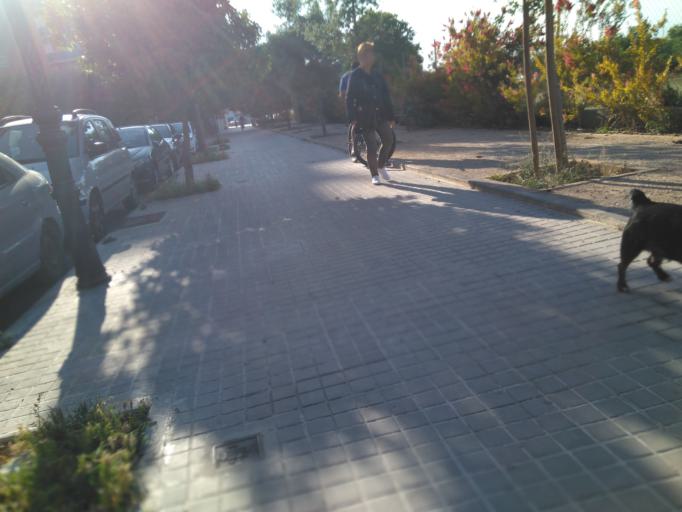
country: ES
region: Valencia
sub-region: Provincia de Valencia
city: Tavernes Blanques
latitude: 39.4974
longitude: -0.3722
